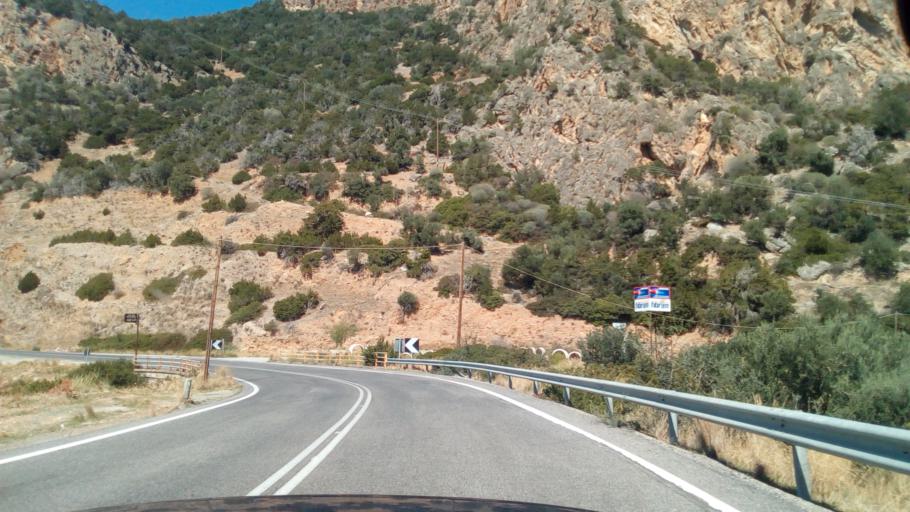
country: GR
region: West Greece
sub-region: Nomos Achaias
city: Aigio
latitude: 38.3582
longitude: 22.1396
